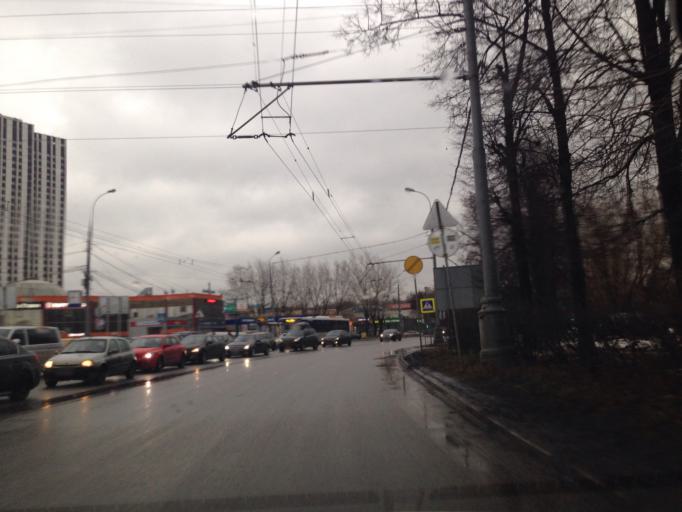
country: RU
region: Moskovskaya
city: Bogorodskoye
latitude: 55.7876
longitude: 37.7466
